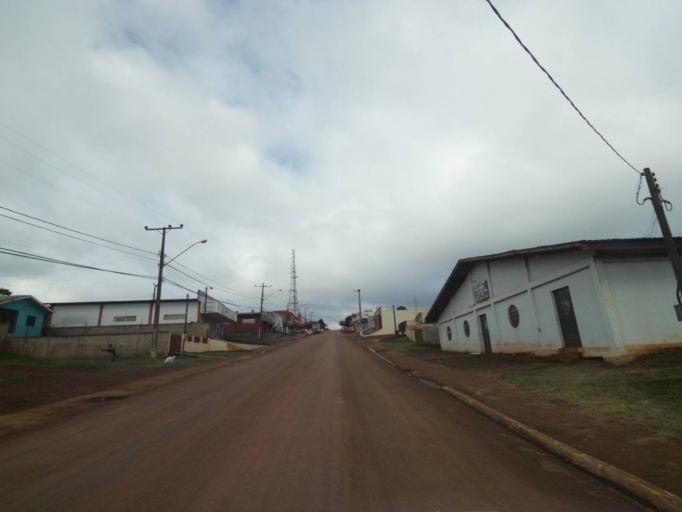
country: BR
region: Parana
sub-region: Pitanga
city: Pitanga
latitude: -24.9404
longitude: -51.8687
